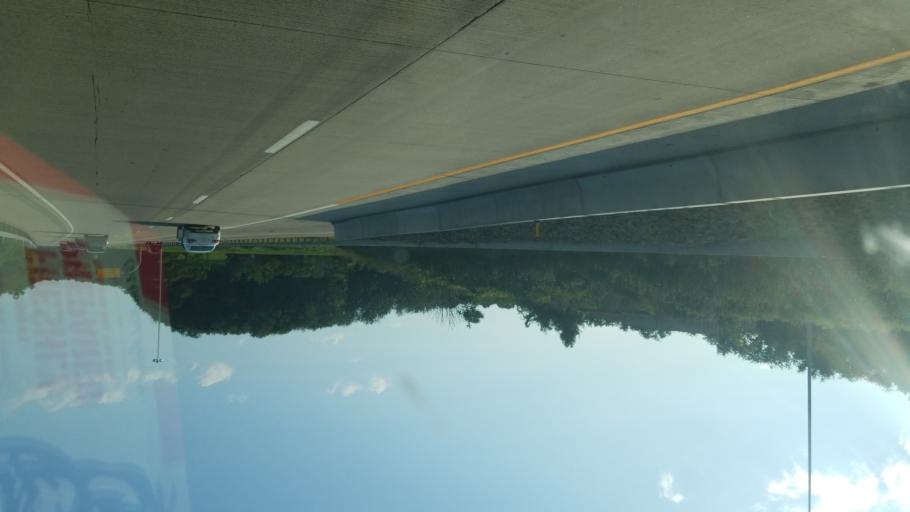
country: US
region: Pennsylvania
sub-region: Washington County
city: Washington
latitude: 40.1908
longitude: -80.2457
